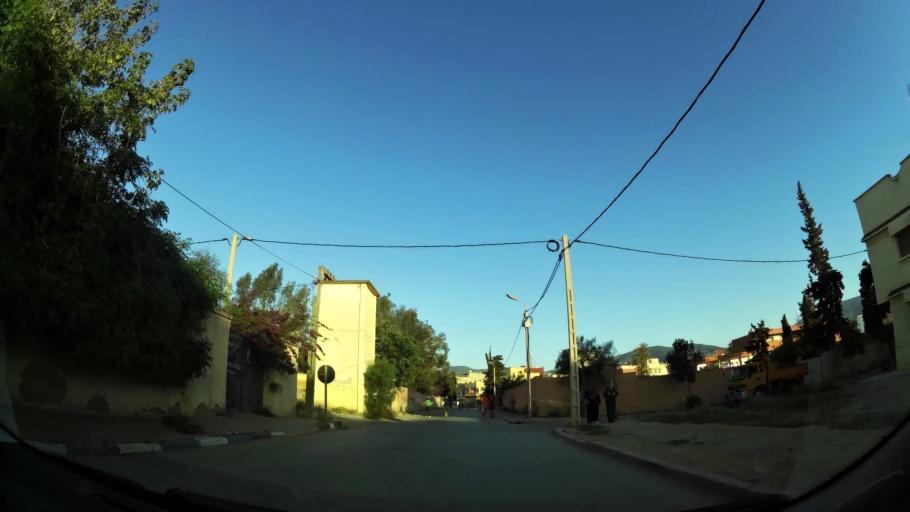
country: MA
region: Oriental
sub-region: Berkane-Taourirt
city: Berkane
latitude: 34.9249
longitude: -2.3272
